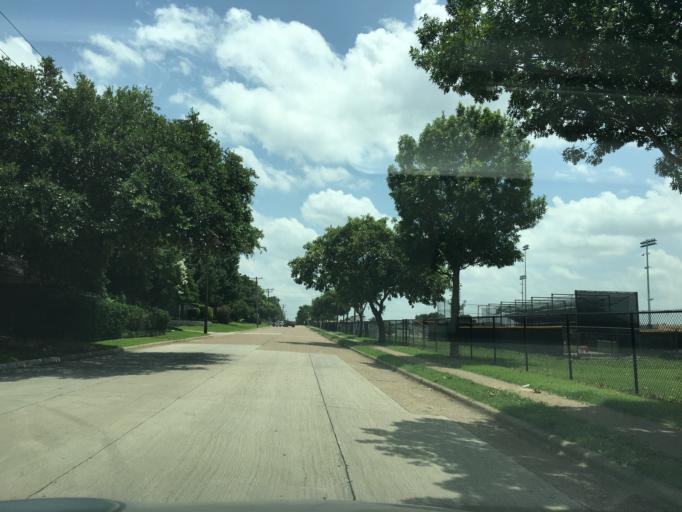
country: US
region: Texas
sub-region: Dallas County
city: University Park
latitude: 32.8869
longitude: -96.7828
